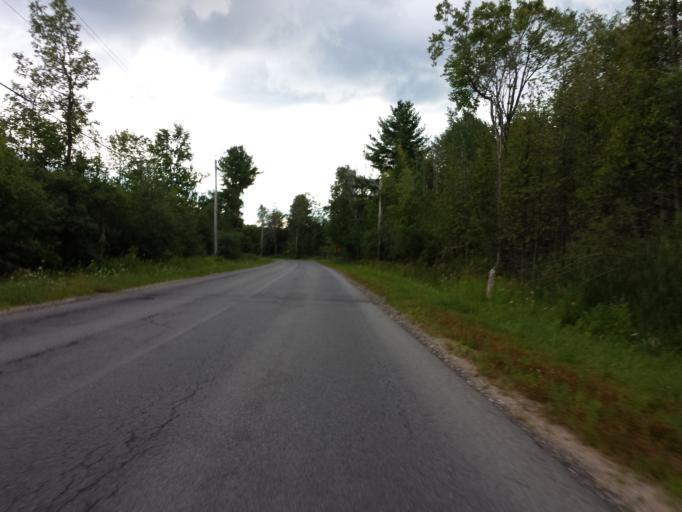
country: US
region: New York
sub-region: St. Lawrence County
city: Potsdam
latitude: 44.6902
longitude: -75.0143
